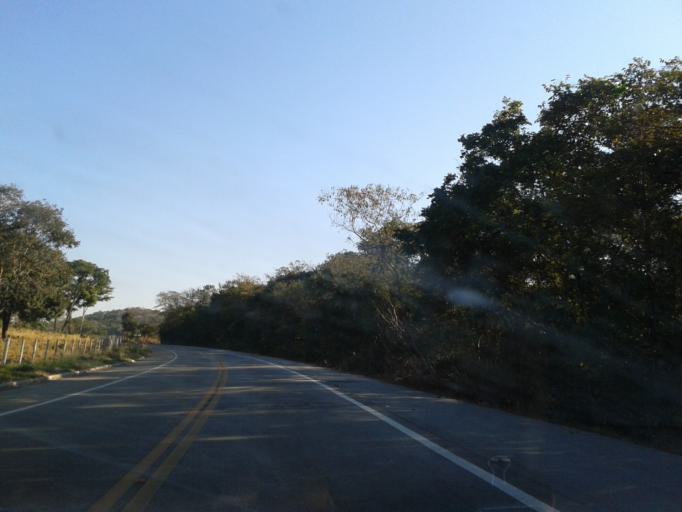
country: BR
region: Goias
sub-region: Itapirapua
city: Itapirapua
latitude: -15.3070
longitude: -50.4436
